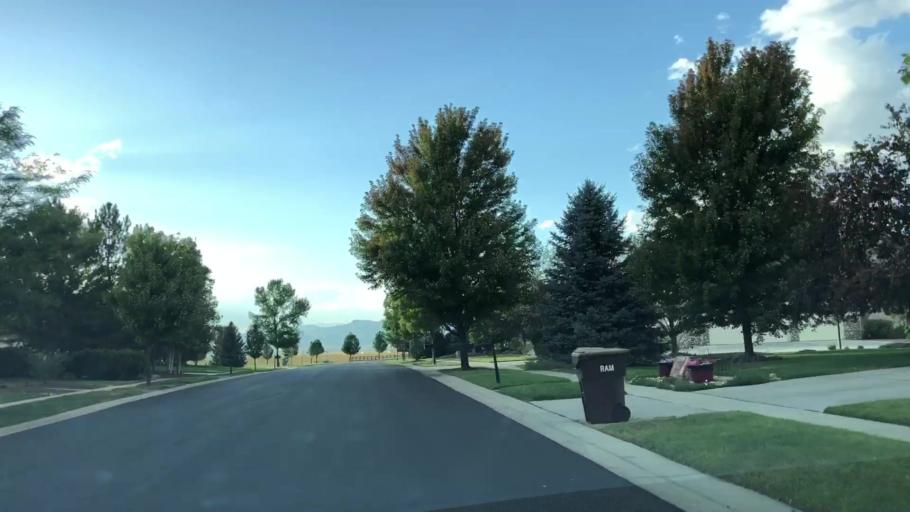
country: US
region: Colorado
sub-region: Weld County
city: Windsor
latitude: 40.4765
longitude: -105.0054
